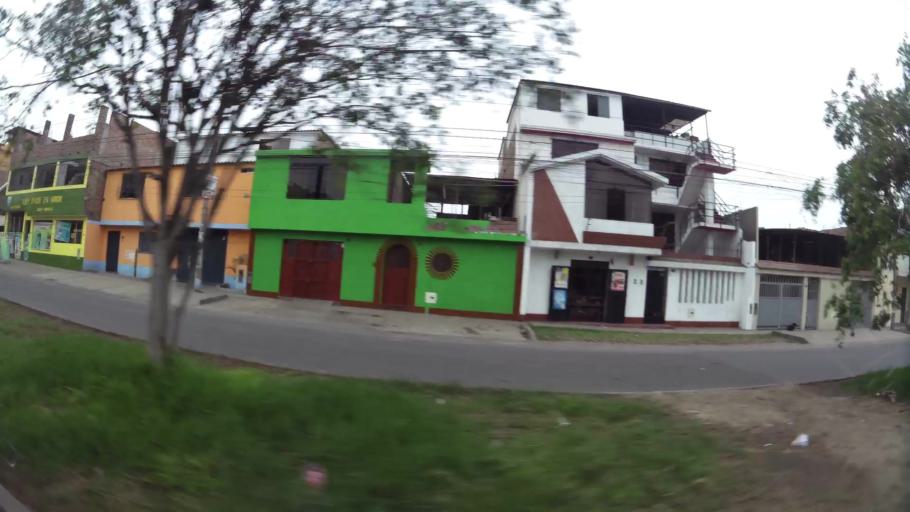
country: PE
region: Lima
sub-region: Lima
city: Surco
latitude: -12.1704
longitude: -76.9709
